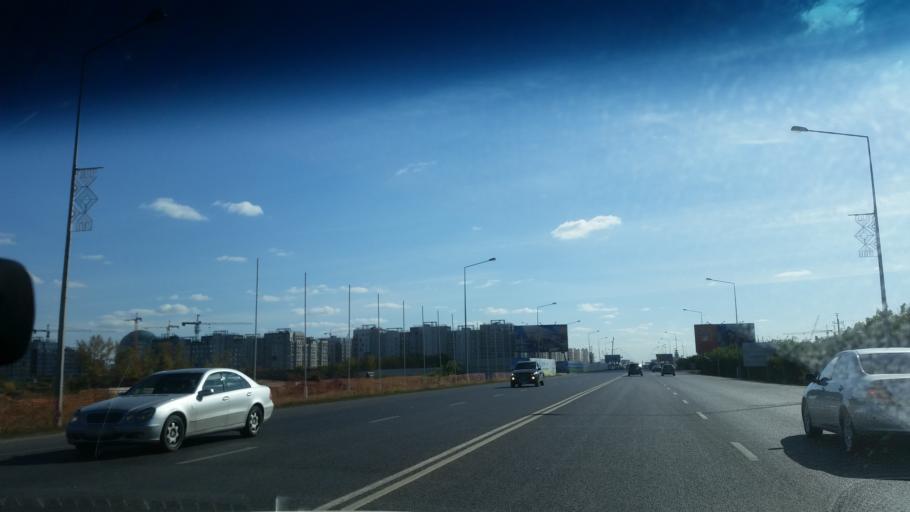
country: KZ
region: Astana Qalasy
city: Astana
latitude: 51.1021
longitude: 71.4073
